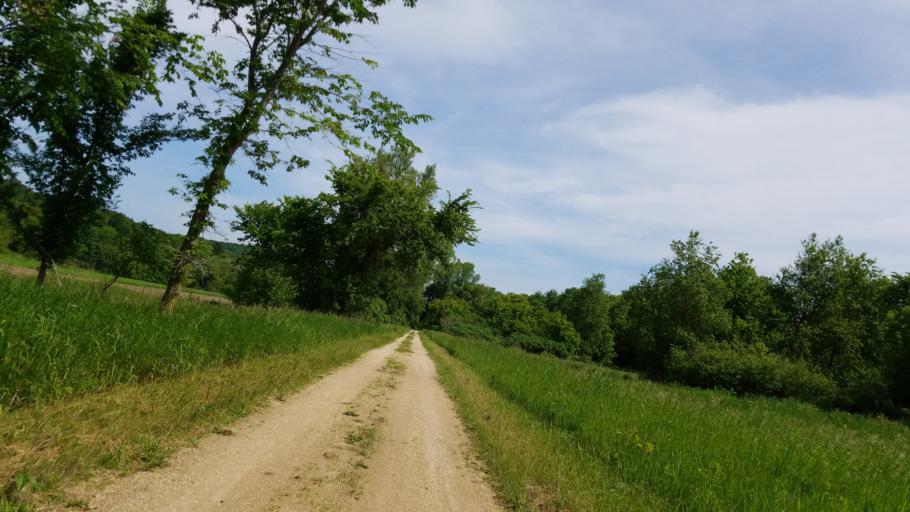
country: US
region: Wisconsin
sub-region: Dunn County
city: Menomonie
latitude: 44.7927
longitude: -91.9469
